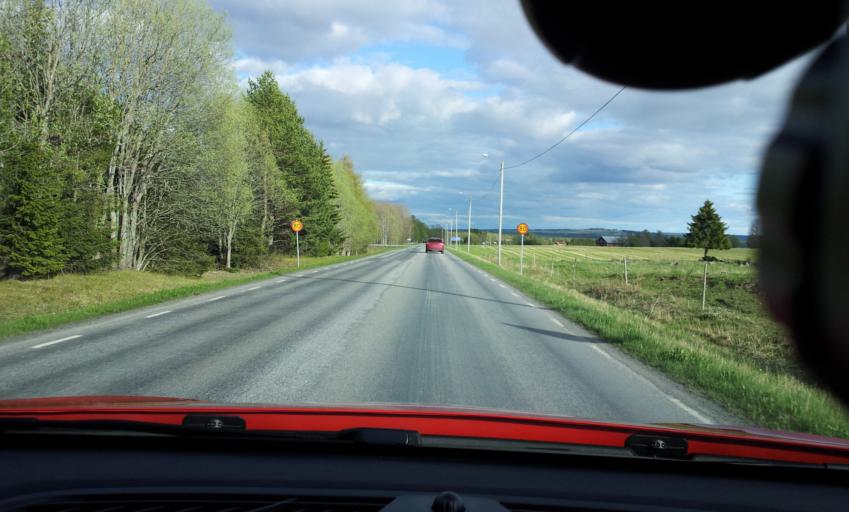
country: SE
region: Jaemtland
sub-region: Krokoms Kommun
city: Krokom
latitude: 63.2490
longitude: 14.4209
